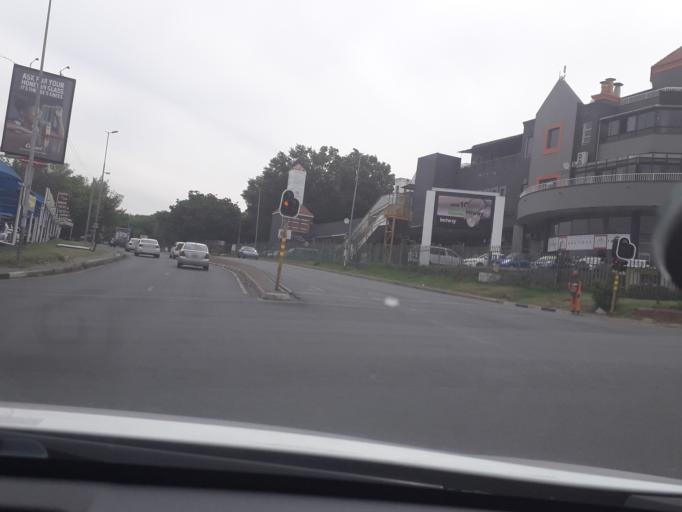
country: ZA
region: Gauteng
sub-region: City of Johannesburg Metropolitan Municipality
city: Johannesburg
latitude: -26.0990
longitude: 28.0107
